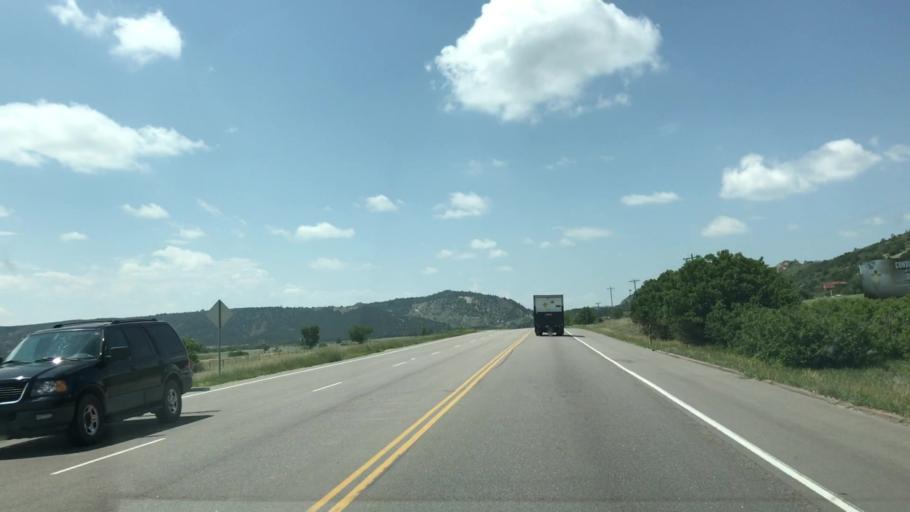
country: US
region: Colorado
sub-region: El Paso County
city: Fort Carson
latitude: 38.6900
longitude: -104.8386
